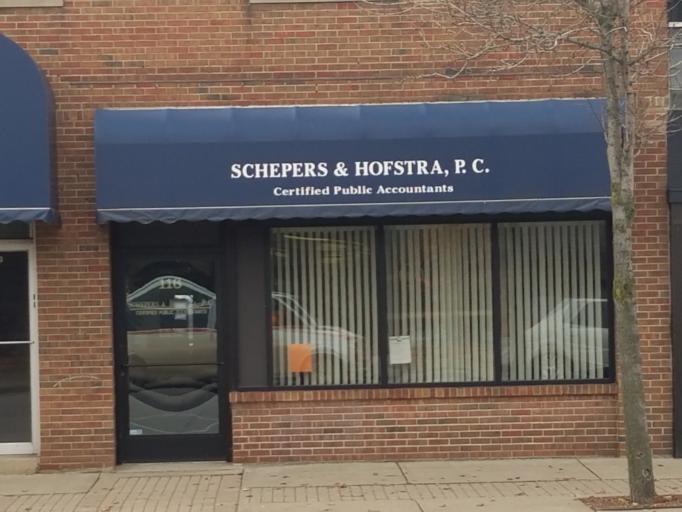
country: US
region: Michigan
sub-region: Wexford County
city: Cadillac
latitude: 44.2497
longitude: -85.3989
